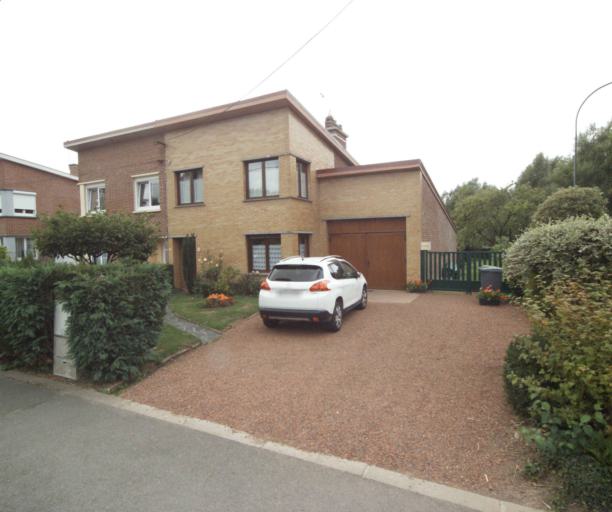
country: FR
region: Nord-Pas-de-Calais
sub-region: Departement du Nord
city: Gruson
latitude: 50.5990
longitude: 3.2009
